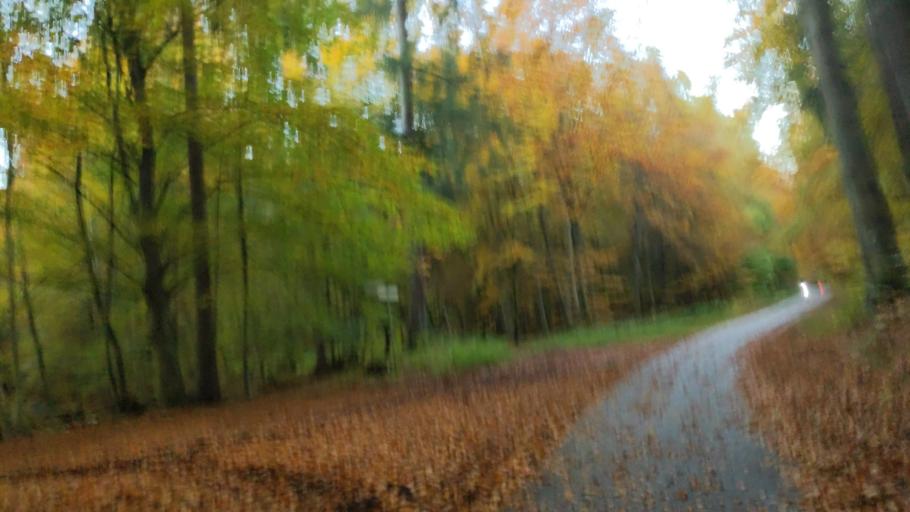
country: DE
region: Schleswig-Holstein
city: Bad Schwartau
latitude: 53.8847
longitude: 10.7504
